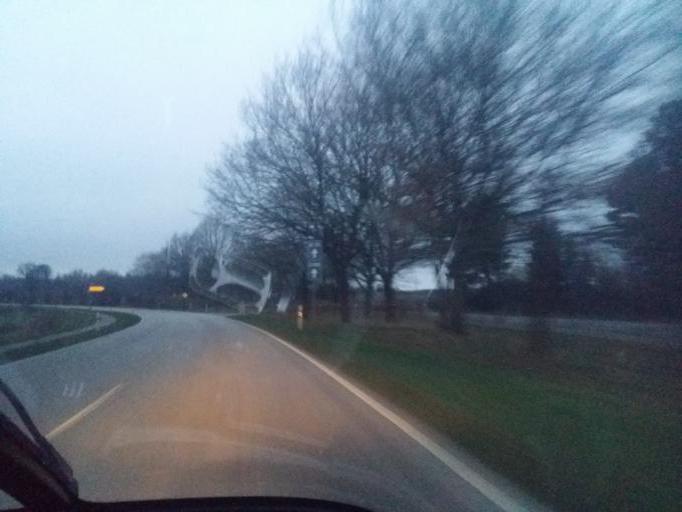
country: DE
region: Schleswig-Holstein
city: Warringholz
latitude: 54.0792
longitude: 9.4632
